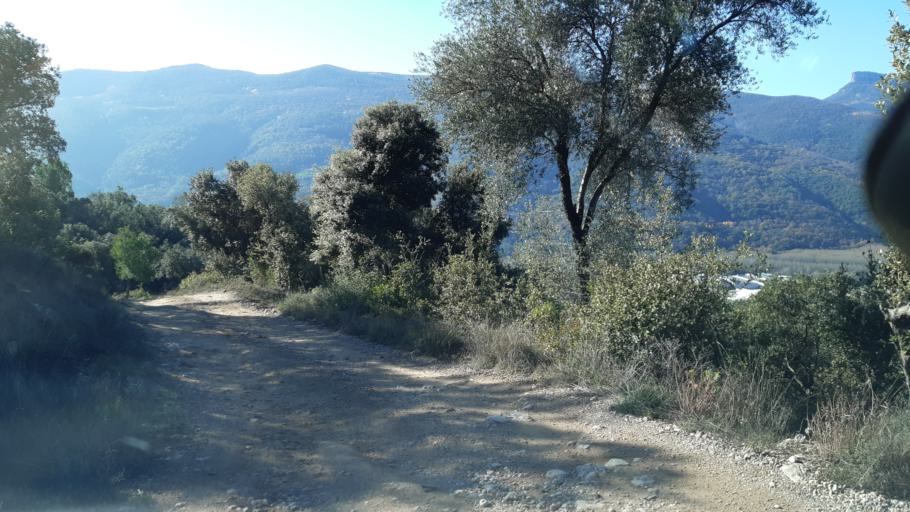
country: ES
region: Catalonia
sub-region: Provincia de Girona
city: la Cellera de Ter
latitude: 42.0209
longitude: 2.6074
